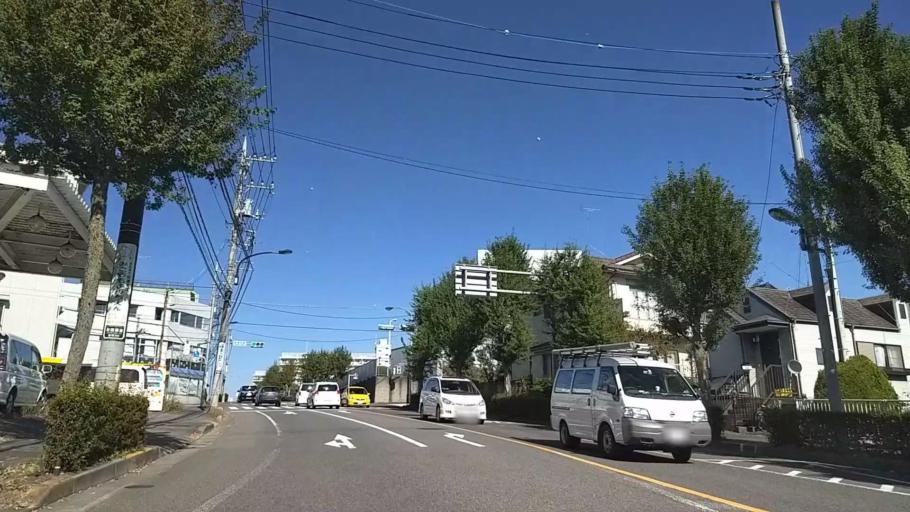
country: JP
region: Tokyo
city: Hachioji
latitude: 35.6352
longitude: 139.2877
